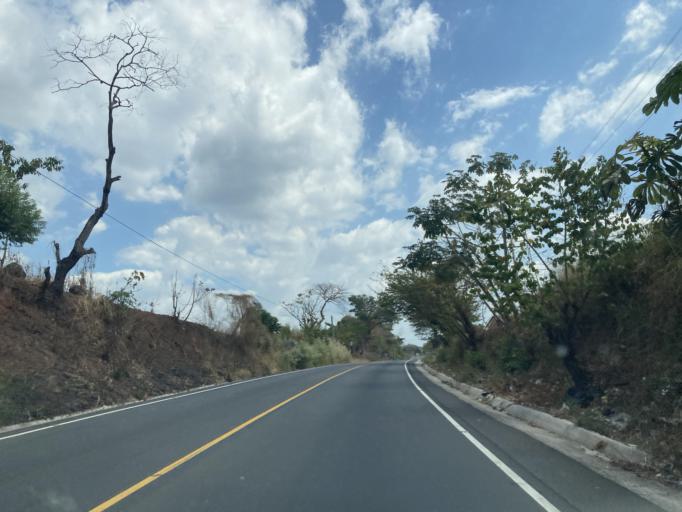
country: GT
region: Santa Rosa
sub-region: Municipio de Taxisco
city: Taxisco
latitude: 14.0634
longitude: -90.4637
